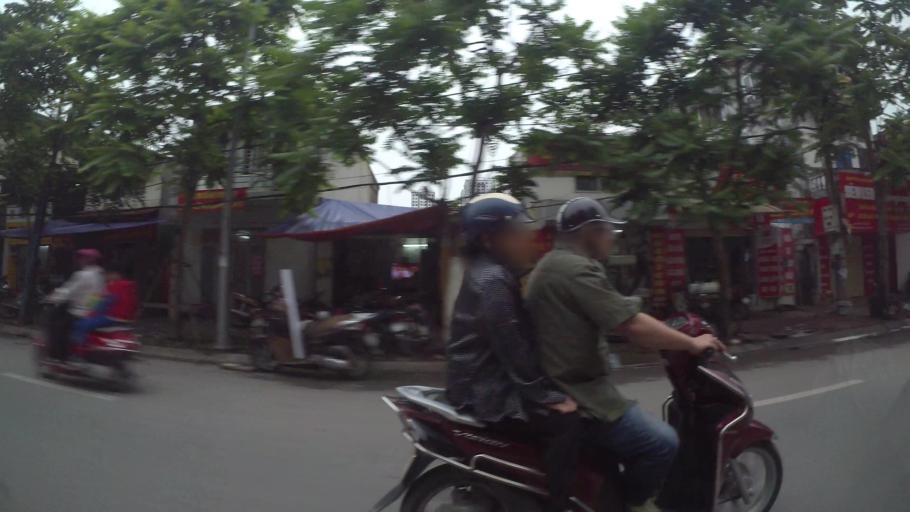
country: VN
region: Ha Noi
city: Hai BaTrung
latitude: 20.9950
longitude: 105.8740
